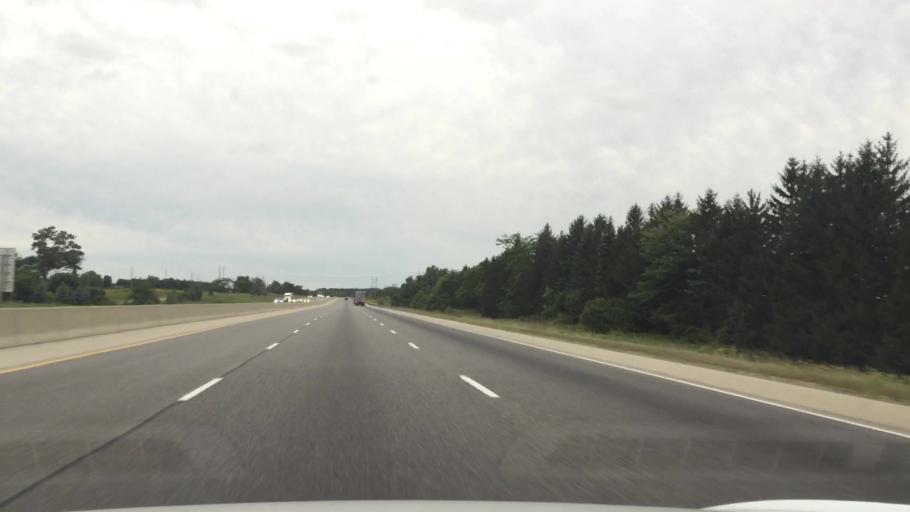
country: CA
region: Ontario
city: Kitchener
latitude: 43.2827
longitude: -80.5167
